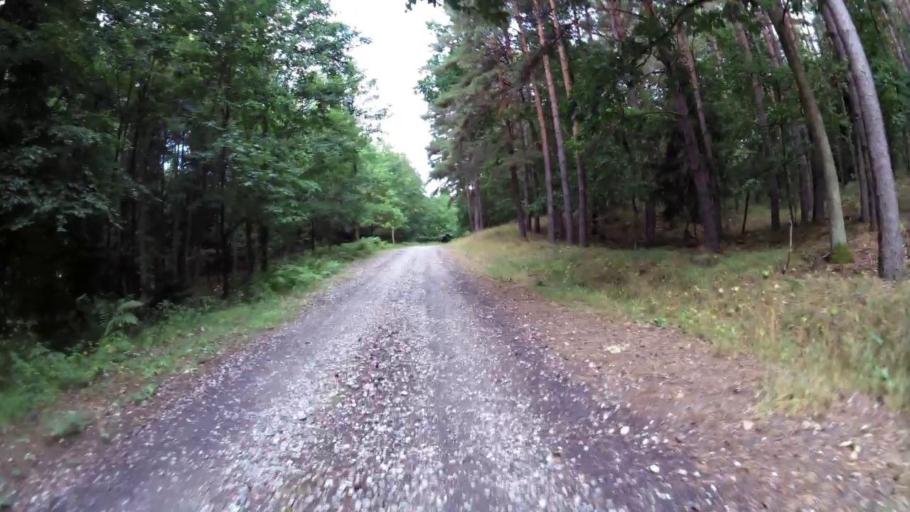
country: PL
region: West Pomeranian Voivodeship
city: Trzcinsko Zdroj
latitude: 52.8856
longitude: 14.6799
